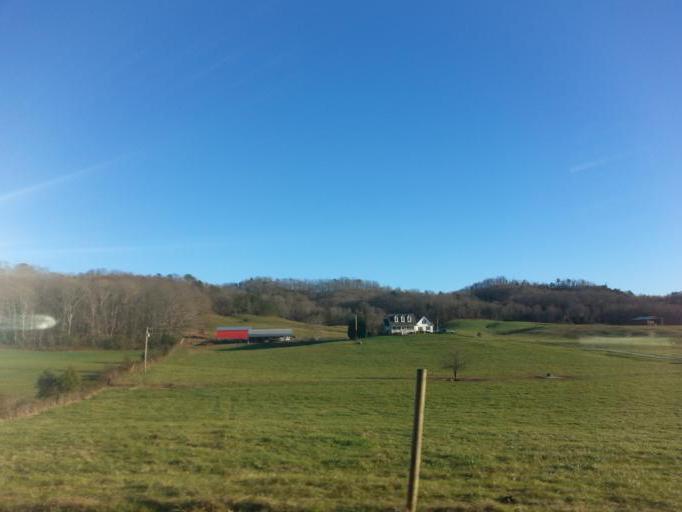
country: US
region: Tennessee
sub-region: Anderson County
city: Clinton
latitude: 36.1369
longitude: -84.1892
